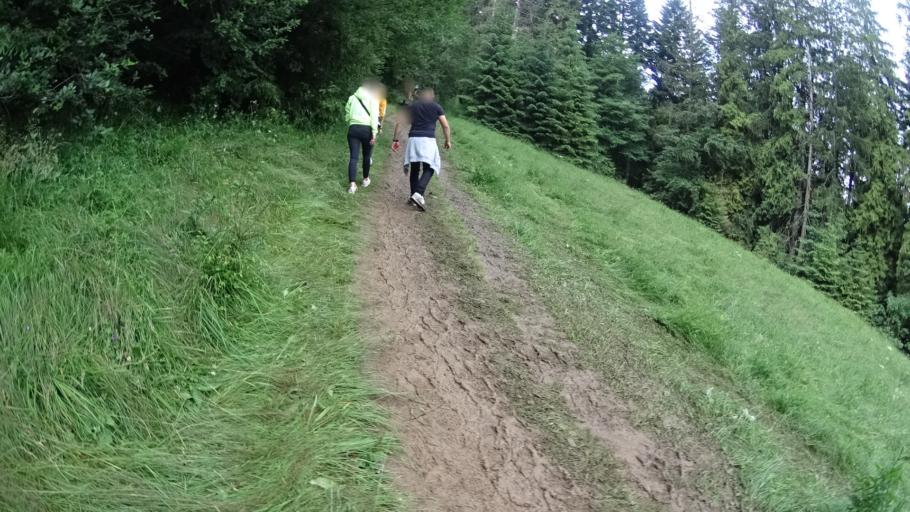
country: PL
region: Lesser Poland Voivodeship
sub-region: Powiat tatrzanski
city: Zakopane
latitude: 49.3044
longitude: 19.9421
